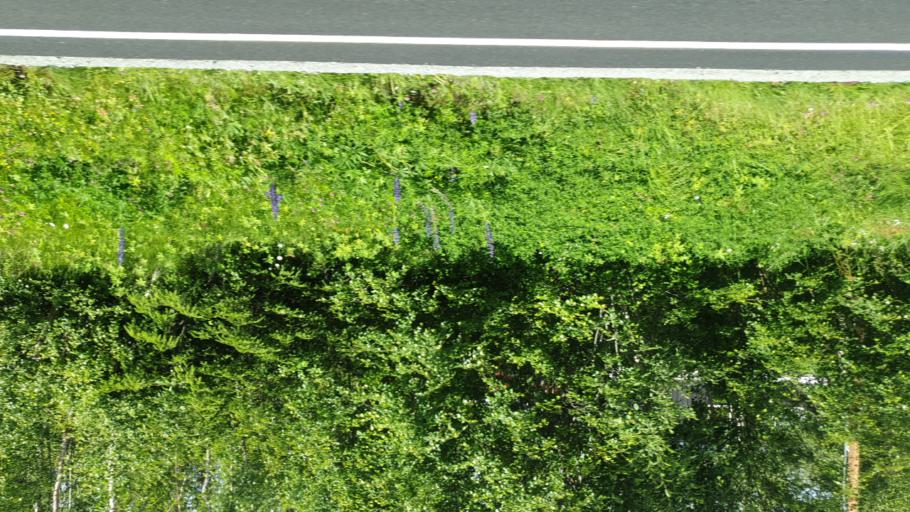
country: NO
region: Oppland
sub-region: Oystre Slidre
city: Heggenes
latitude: 61.1739
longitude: 8.9945
